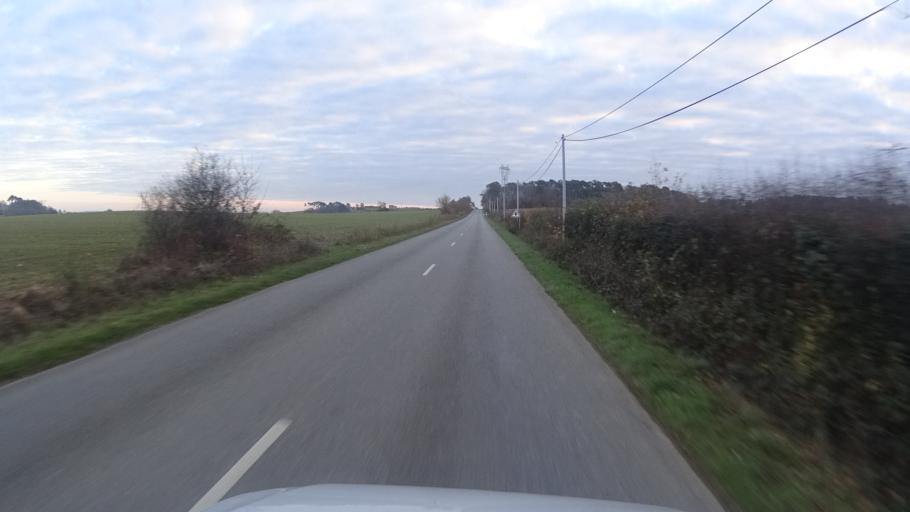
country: FR
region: Pays de la Loire
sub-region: Departement de la Loire-Atlantique
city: Avessac
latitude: 47.6532
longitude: -1.9730
